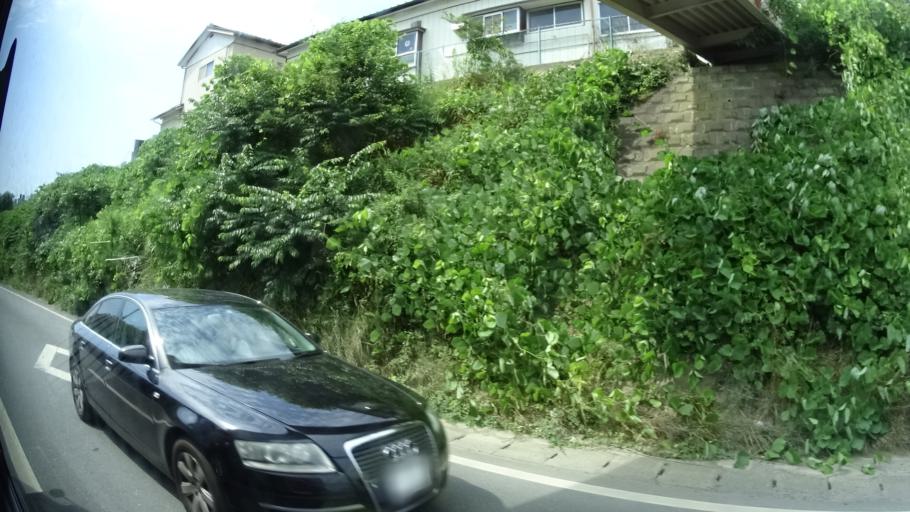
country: JP
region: Iwate
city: Ofunato
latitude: 38.8794
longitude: 141.5766
